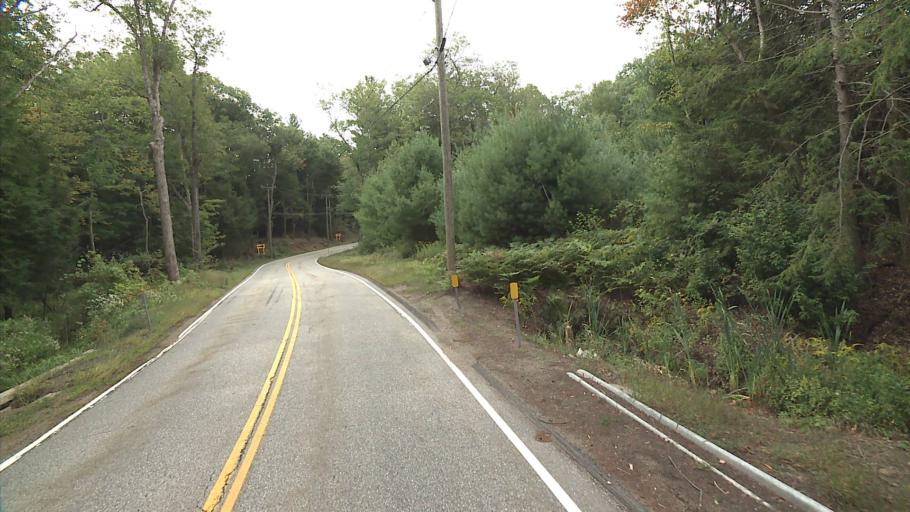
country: US
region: Connecticut
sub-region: Tolland County
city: Stafford Springs
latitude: 41.9150
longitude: -72.2616
